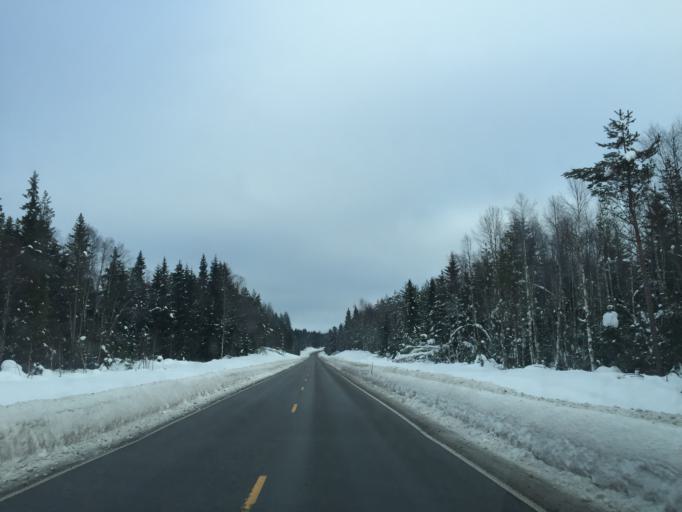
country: NO
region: Hedmark
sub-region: Trysil
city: Innbygda
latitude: 61.1659
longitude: 12.1524
